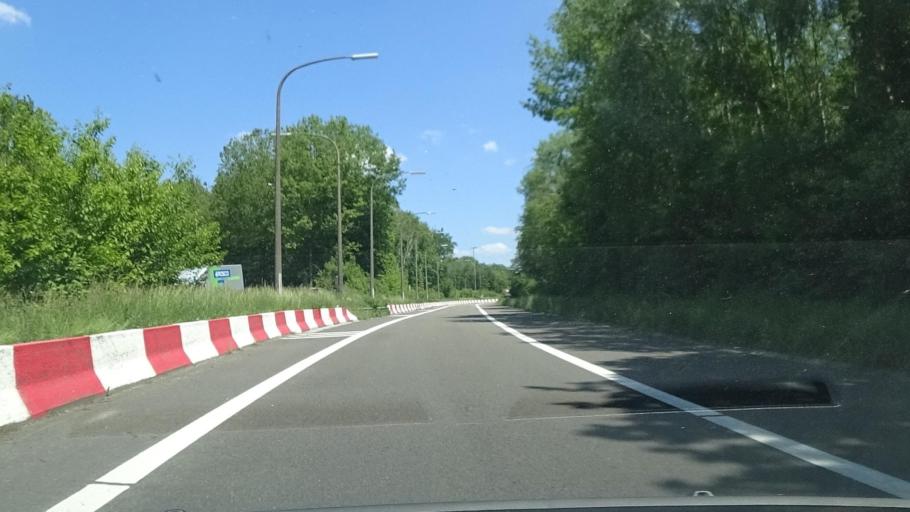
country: BE
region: Wallonia
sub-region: Province du Hainaut
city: La Louviere
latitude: 50.5205
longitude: 4.1971
